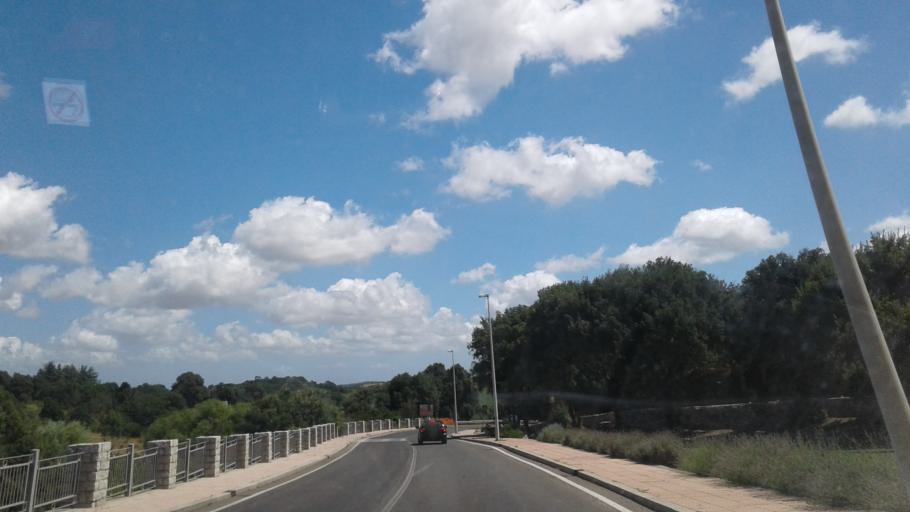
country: IT
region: Sardinia
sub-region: Provincia di Olbia-Tempio
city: Tempio Pausania
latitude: 40.9046
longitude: 9.1133
